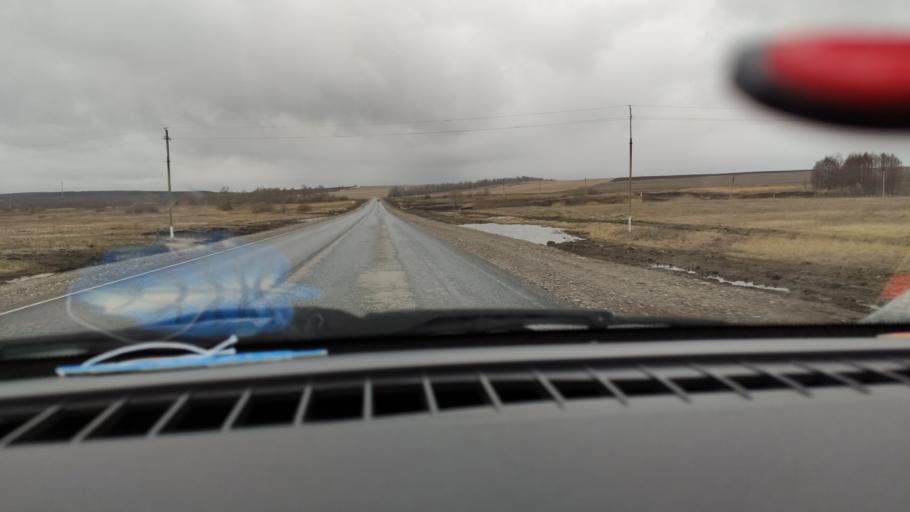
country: RU
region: Tatarstan
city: Cheremshan
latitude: 54.7898
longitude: 51.4448
